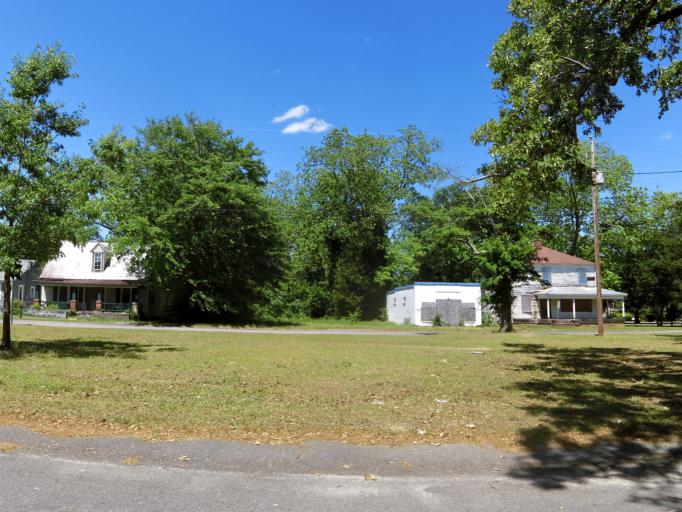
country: US
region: South Carolina
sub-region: Aiken County
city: Aiken
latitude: 33.5627
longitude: -81.7127
